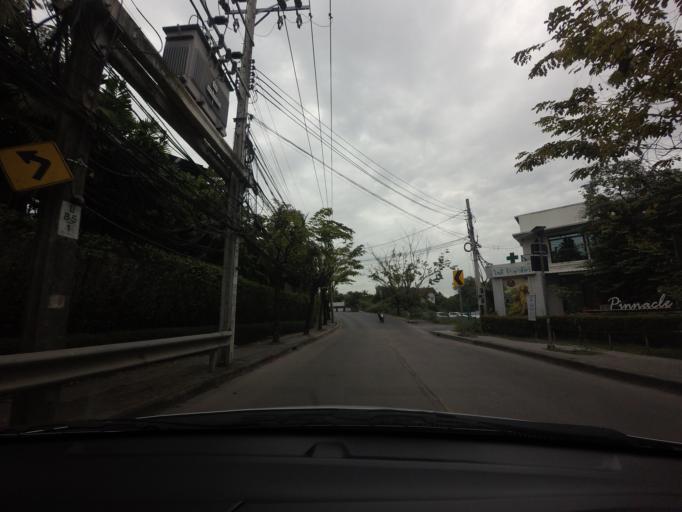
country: TH
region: Bangkok
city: Chom Thong
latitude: 13.6593
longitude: 100.4686
